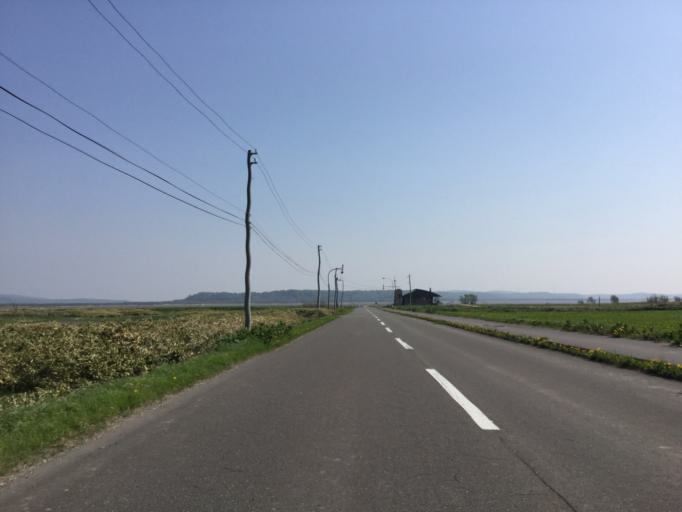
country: JP
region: Hokkaido
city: Makubetsu
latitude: 45.3929
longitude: 141.7673
